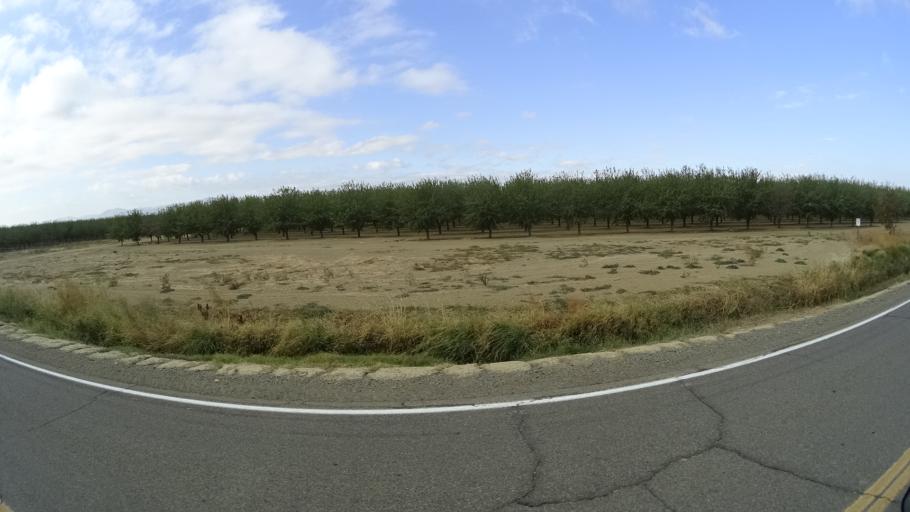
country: US
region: California
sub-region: Yolo County
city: Esparto
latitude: 38.7370
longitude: -122.0061
